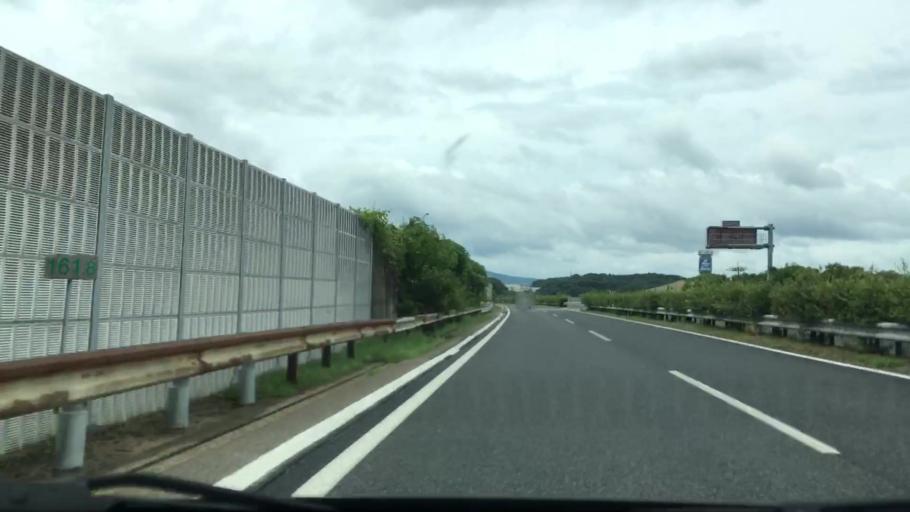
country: JP
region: Okayama
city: Tsuyama
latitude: 35.0644
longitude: 133.9456
